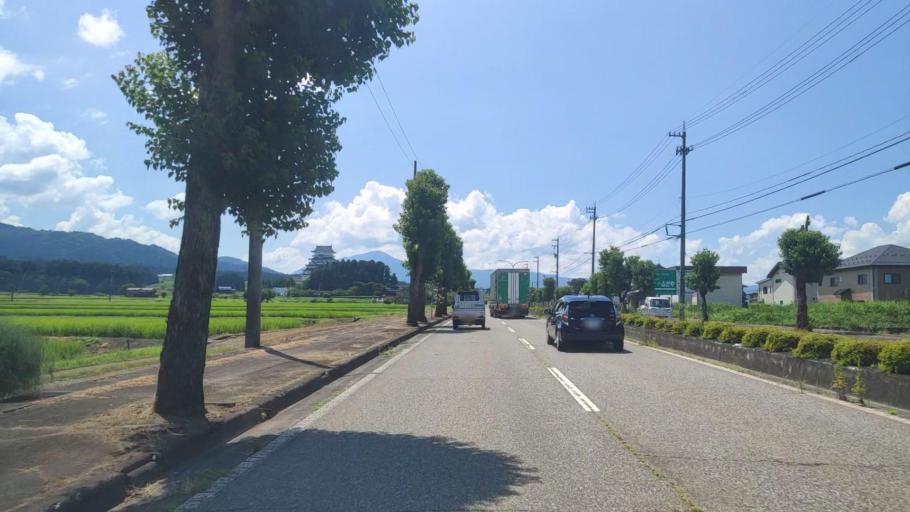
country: JP
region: Fukui
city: Katsuyama
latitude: 36.0486
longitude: 136.5154
